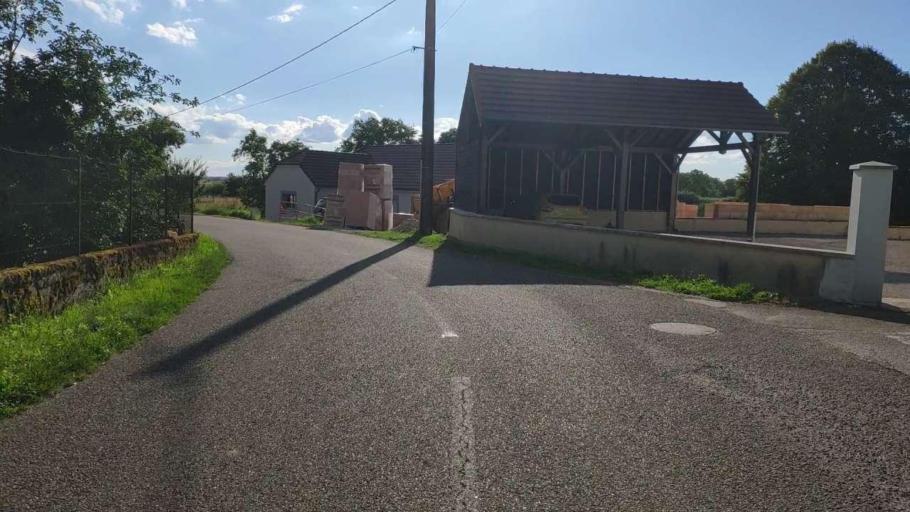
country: FR
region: Franche-Comte
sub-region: Departement du Jura
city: Bletterans
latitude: 46.7628
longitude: 5.5229
